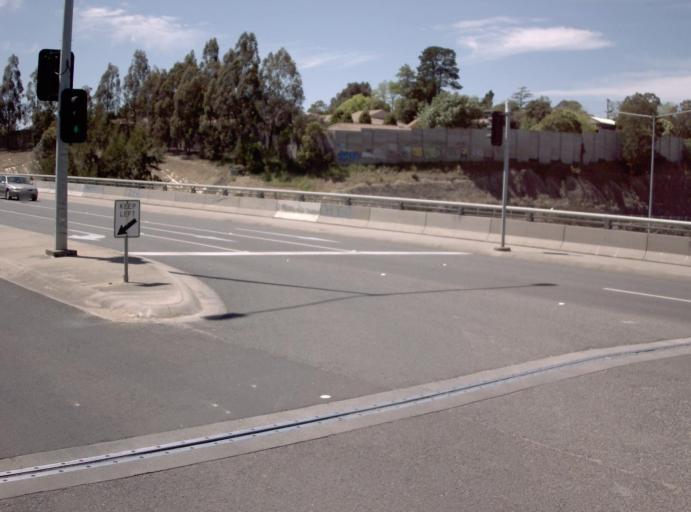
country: AU
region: Victoria
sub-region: Whitehorse
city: Blackburn North
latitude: -37.8017
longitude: 145.1595
